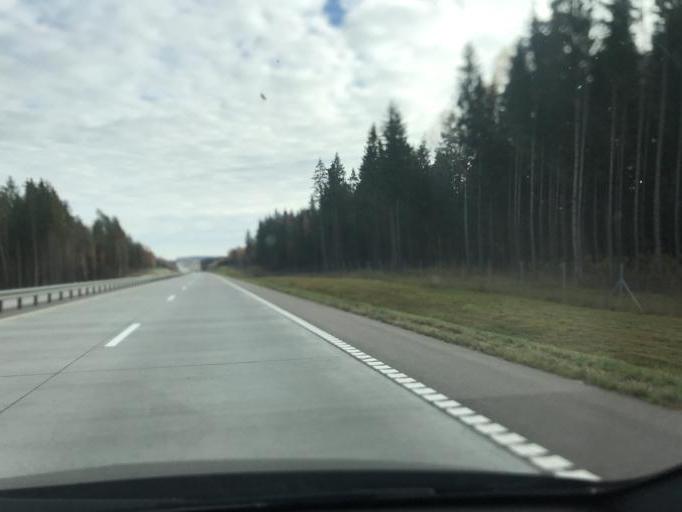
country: BY
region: Minsk
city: Zaslawye
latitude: 54.0646
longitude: 27.3214
